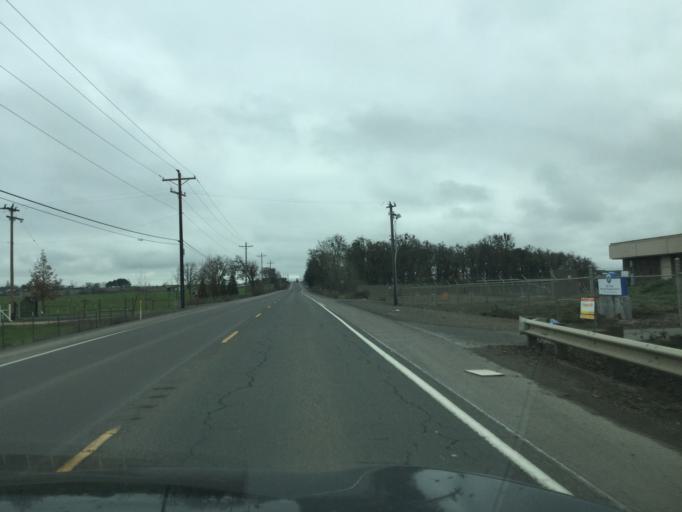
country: US
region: Oregon
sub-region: Jackson County
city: Central Point
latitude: 42.4279
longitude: -122.9475
